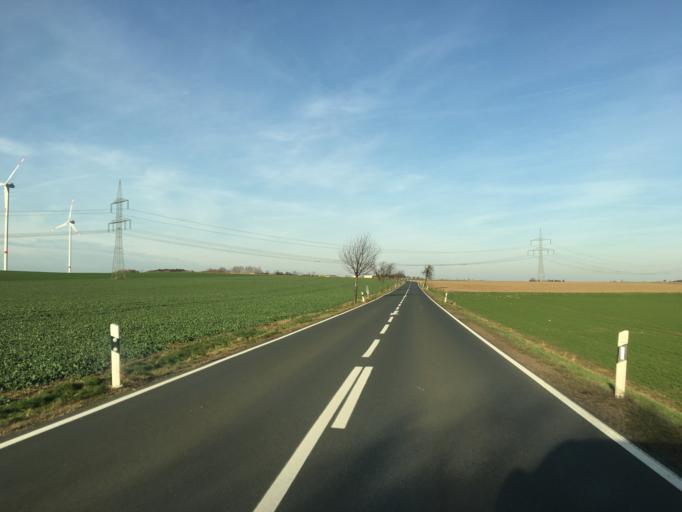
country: DE
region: Saxony
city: Ostrau
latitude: 51.2414
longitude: 13.1677
